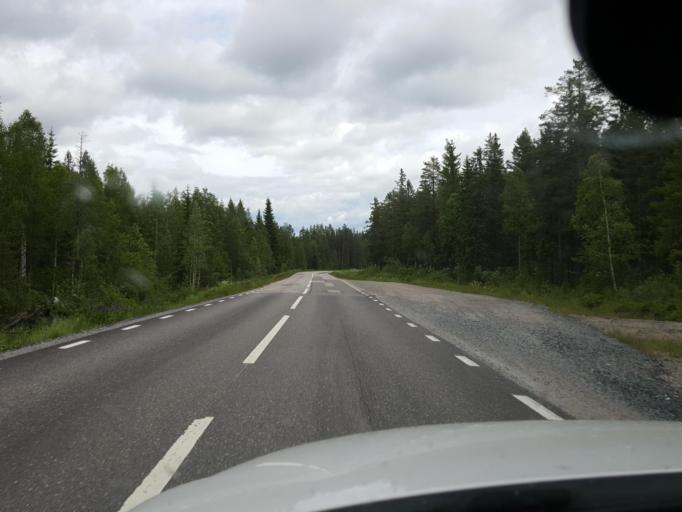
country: SE
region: Gaevleborg
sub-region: Ljusdals Kommun
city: Farila
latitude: 61.7801
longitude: 15.5992
